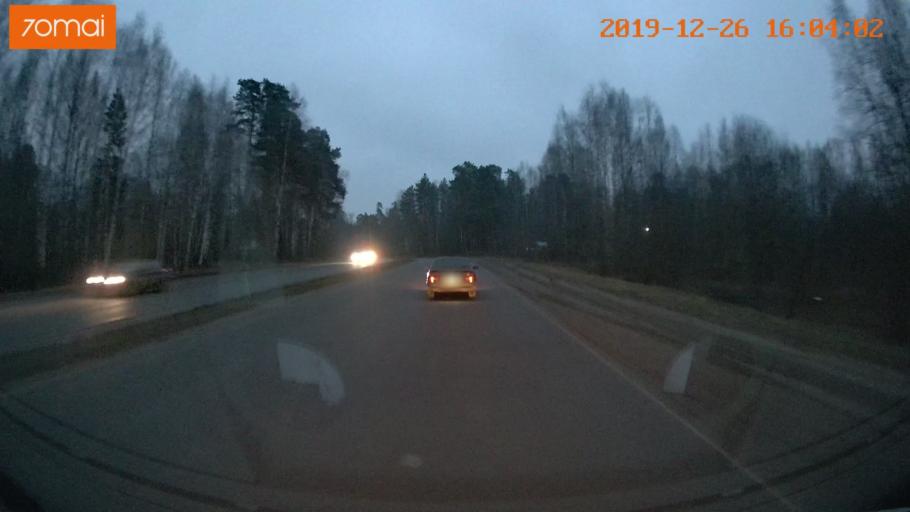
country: RU
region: Jaroslavl
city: Rybinsk
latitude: 58.0092
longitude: 38.8616
